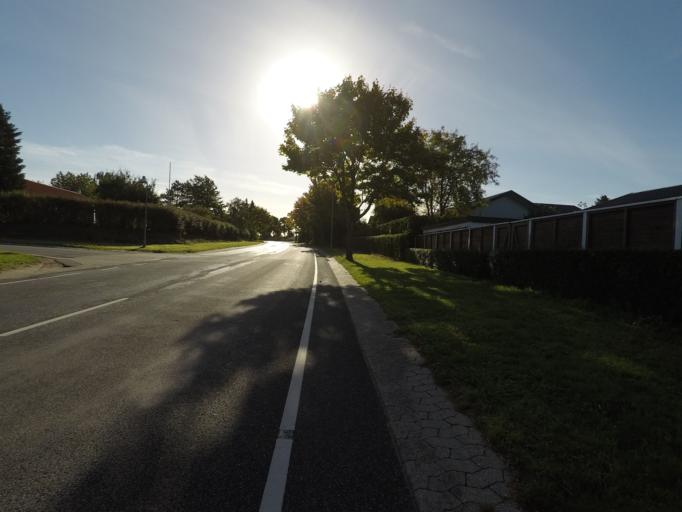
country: DK
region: Capital Region
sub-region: Egedal Kommune
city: Smorumnedre
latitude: 55.7381
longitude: 12.3024
